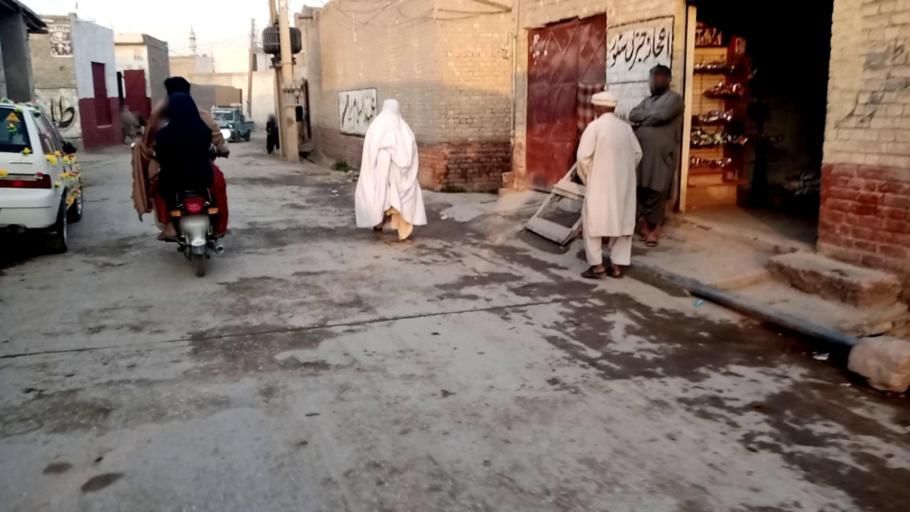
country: PK
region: Khyber Pakhtunkhwa
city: Peshawar
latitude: 34.0495
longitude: 71.4579
